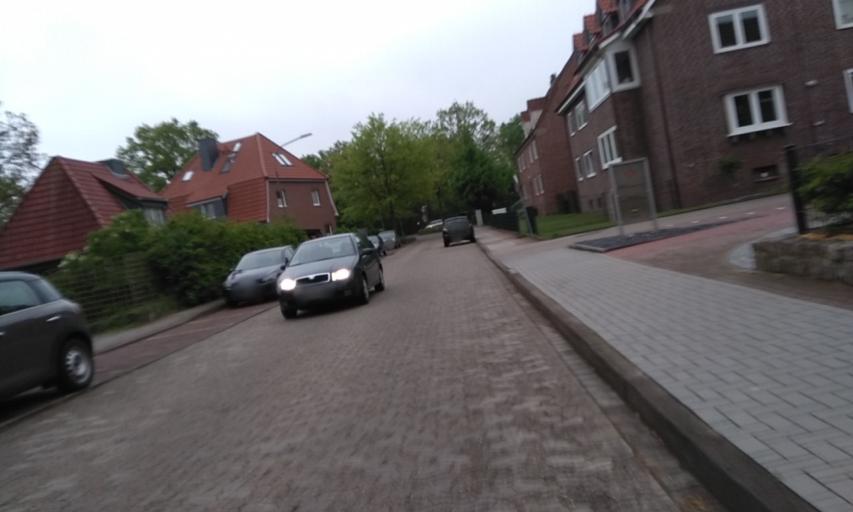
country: DE
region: Lower Saxony
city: Buxtehude
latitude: 53.4683
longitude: 9.6812
